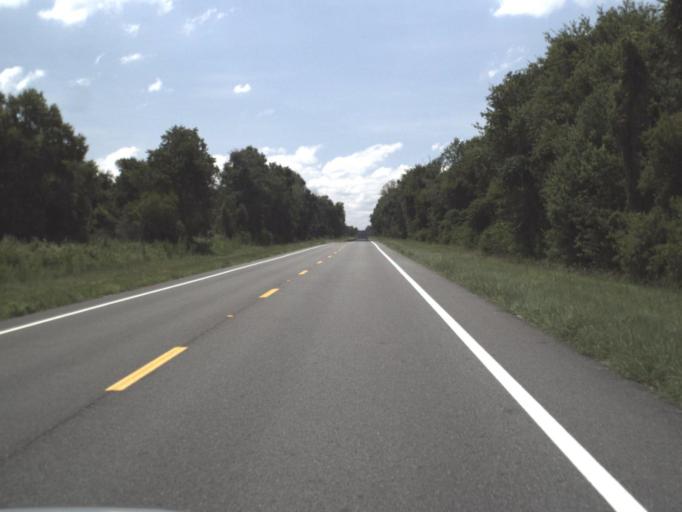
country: US
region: Florida
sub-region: Hamilton County
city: Jasper
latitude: 30.4083
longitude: -82.8434
